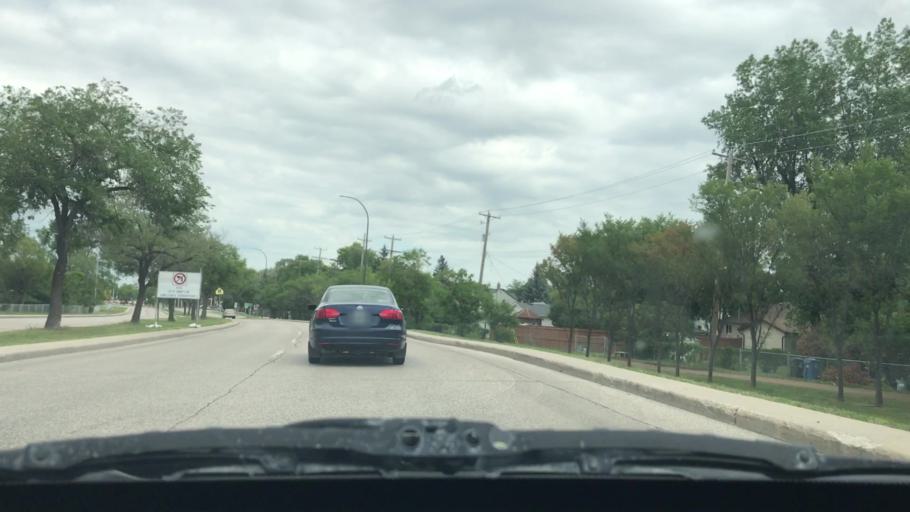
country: CA
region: Manitoba
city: Winnipeg
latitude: 49.8504
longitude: -97.1181
